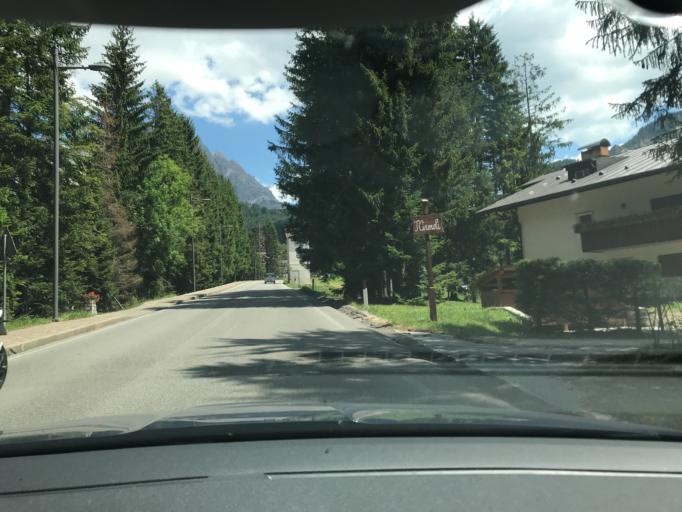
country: IT
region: Veneto
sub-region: Provincia di Belluno
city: Cortina d'Ampezzo
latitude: 46.5429
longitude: 12.1452
